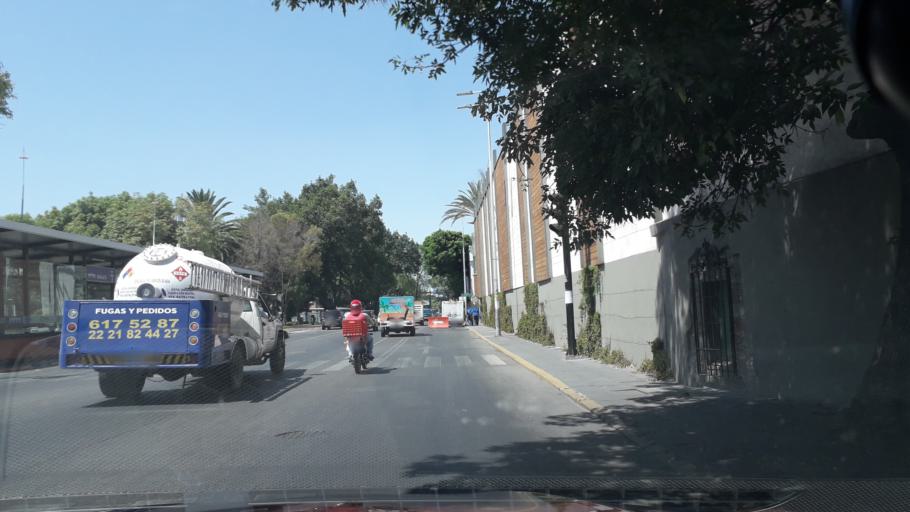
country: MX
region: Puebla
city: Puebla
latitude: 19.0413
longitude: -98.1934
